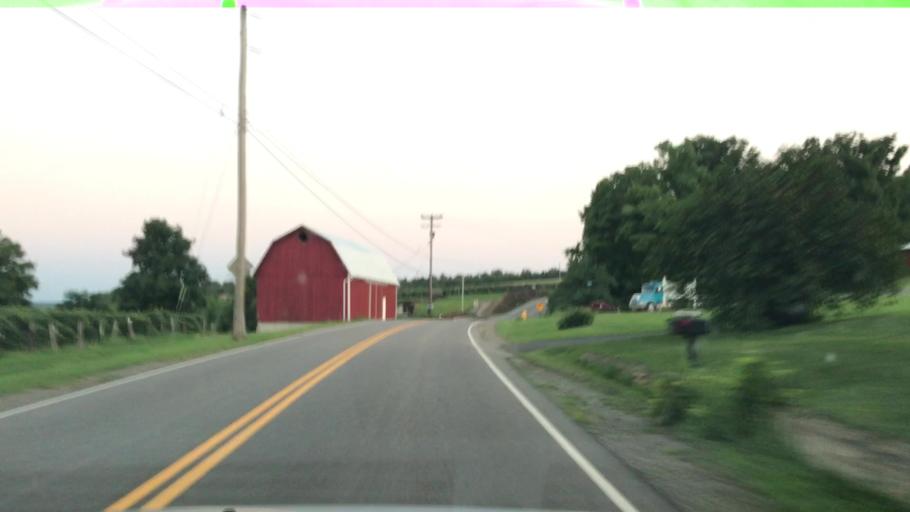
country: US
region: New York
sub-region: Steuben County
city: Sylvan Beach
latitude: 42.5222
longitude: -77.1690
